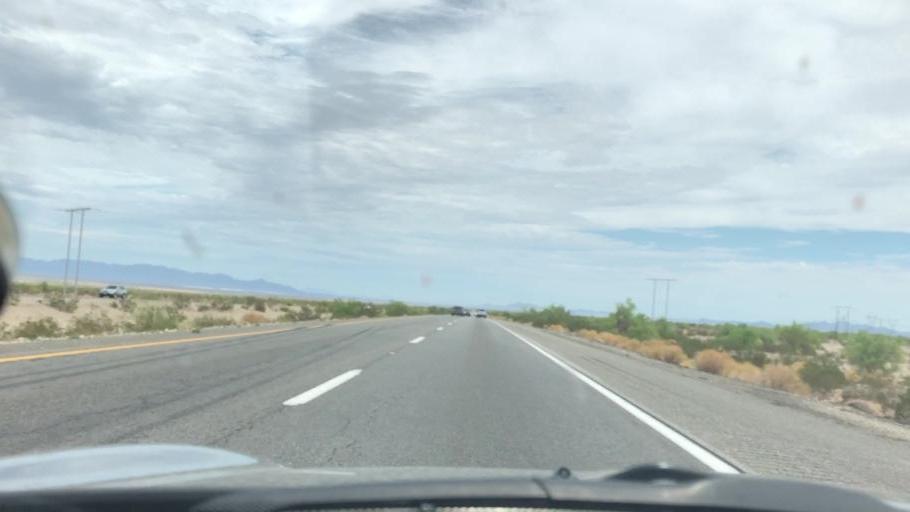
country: US
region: California
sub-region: Riverside County
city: Mesa Verde
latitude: 33.6770
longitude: -115.2262
